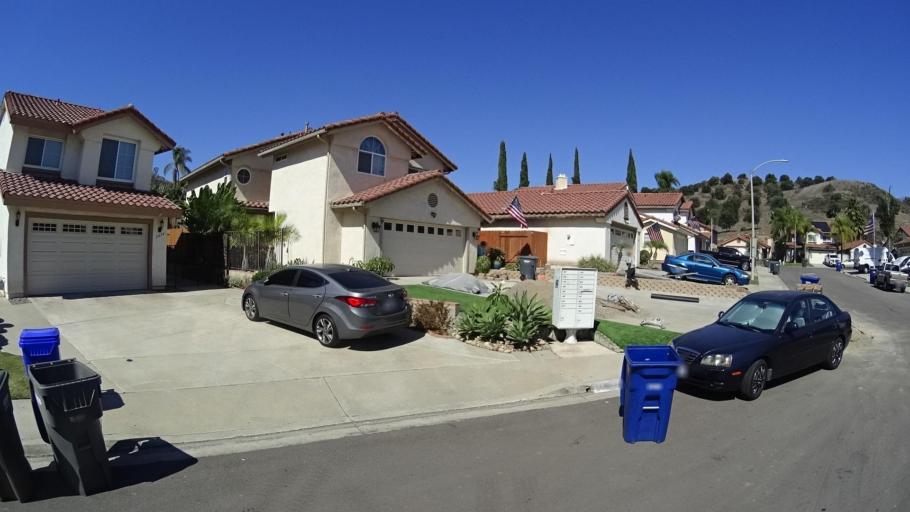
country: US
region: California
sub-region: San Diego County
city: Rancho San Diego
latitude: 32.7501
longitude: -116.9394
